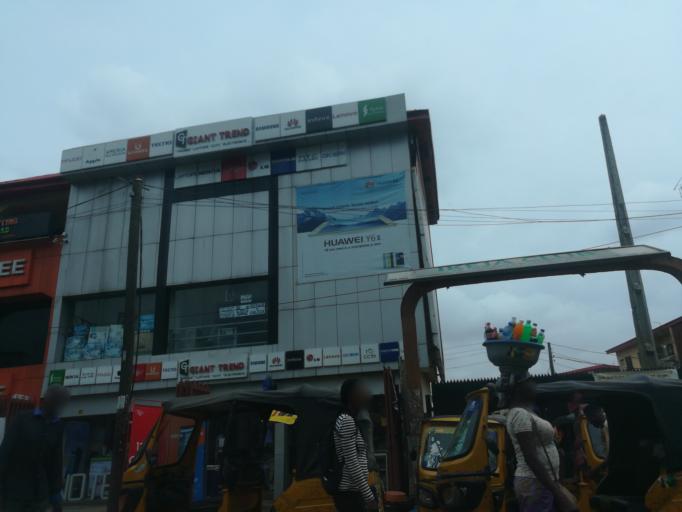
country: NG
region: Lagos
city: Ikeja
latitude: 6.5961
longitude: 3.3393
